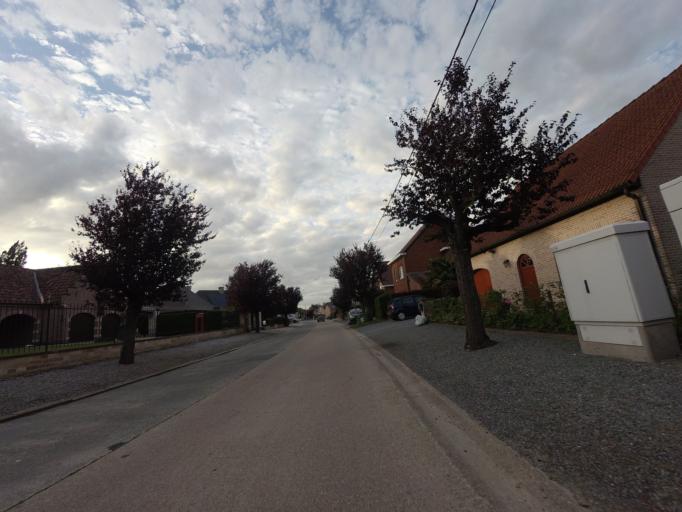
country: BE
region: Flanders
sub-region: Provincie Vlaams-Brabant
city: Grimbergen
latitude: 50.9705
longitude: 4.3609
